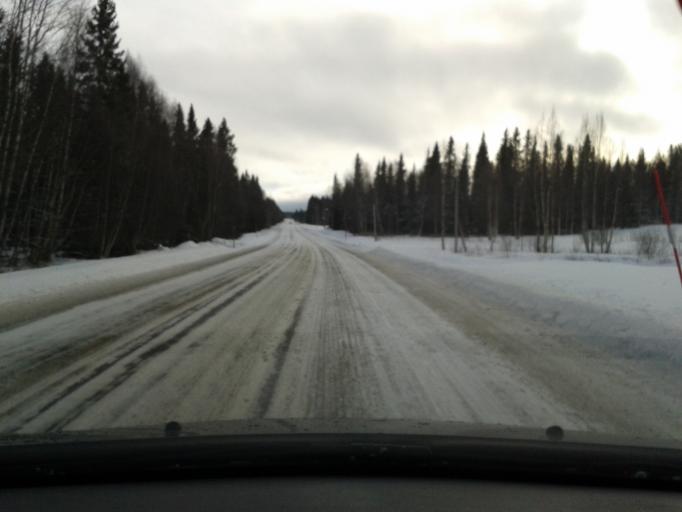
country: SE
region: Vaesterbotten
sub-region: Vilhelmina Kommun
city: Sjoberg
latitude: 64.7218
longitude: 16.2313
